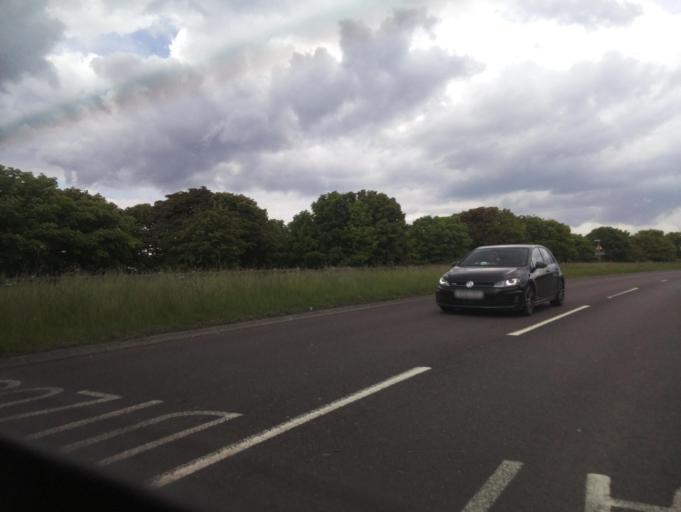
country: GB
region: England
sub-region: County Durham
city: Chester-le-Street
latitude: 54.9035
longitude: -1.5638
